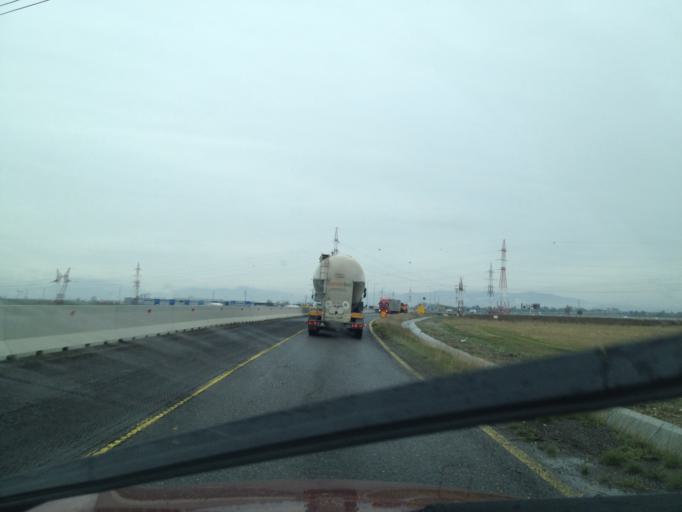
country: RO
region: Brasov
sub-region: Comuna Sanpetru
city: Sanpetru
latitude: 45.6883
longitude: 25.6528
